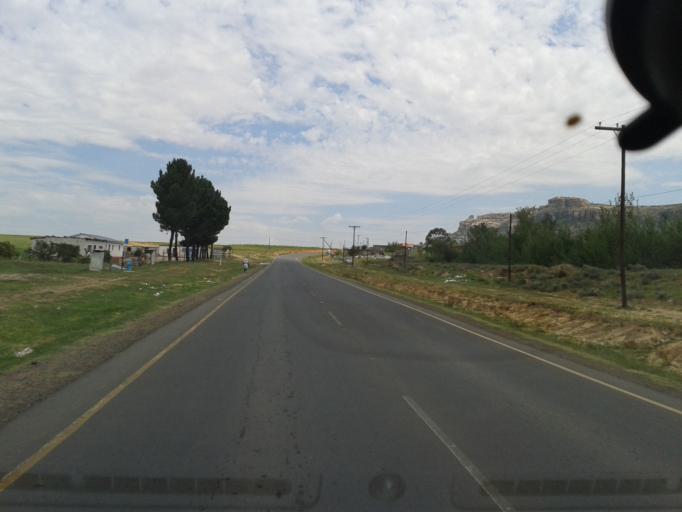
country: LS
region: Maseru
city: Maseru
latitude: -29.3562
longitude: 27.5791
